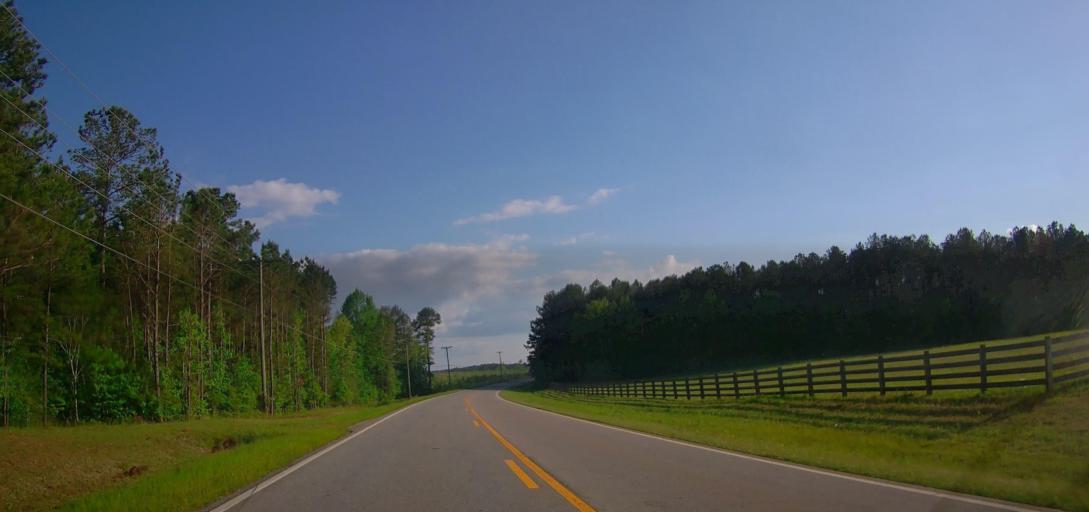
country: US
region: Georgia
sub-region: Putnam County
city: Eatonton
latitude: 33.2582
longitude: -83.3011
